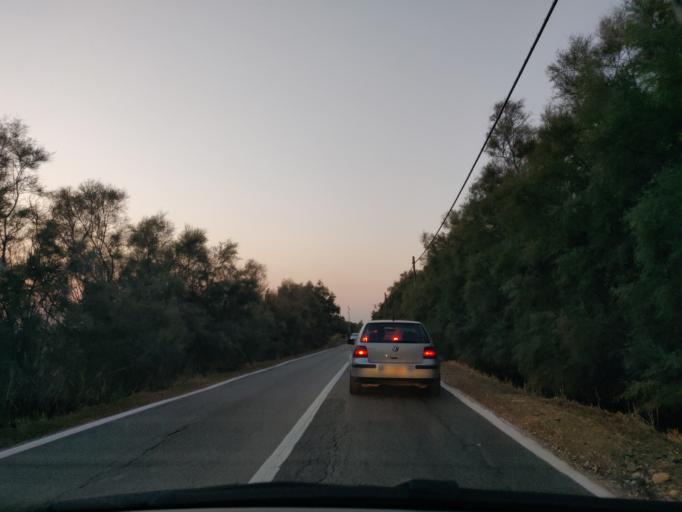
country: IT
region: Latium
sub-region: Citta metropolitana di Roma Capitale
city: Npp 23 (Parco Leonardo)
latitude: 41.8228
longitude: 12.2920
